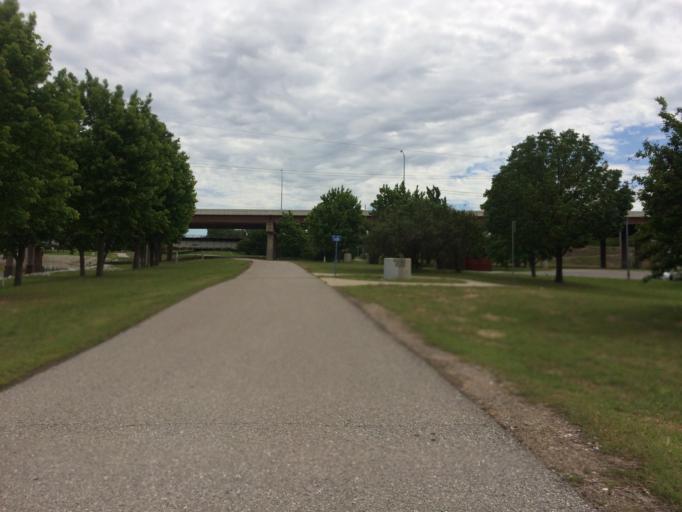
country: US
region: Oklahoma
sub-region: Oklahoma County
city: Oklahoma City
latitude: 35.4474
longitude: -97.5151
